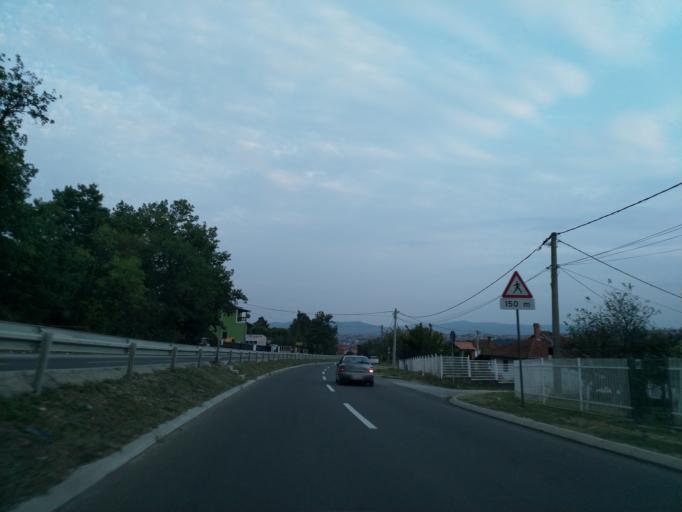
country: RS
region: Central Serbia
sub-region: Sumadijski Okrug
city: Kragujevac
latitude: 44.0559
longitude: 20.8962
